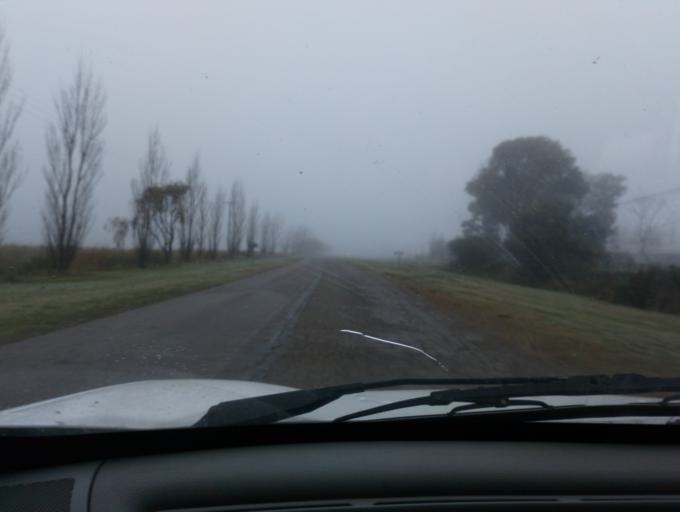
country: AR
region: La Pampa
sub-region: Departamento de Guatrache
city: Guatrache
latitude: -37.6651
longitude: -63.5201
